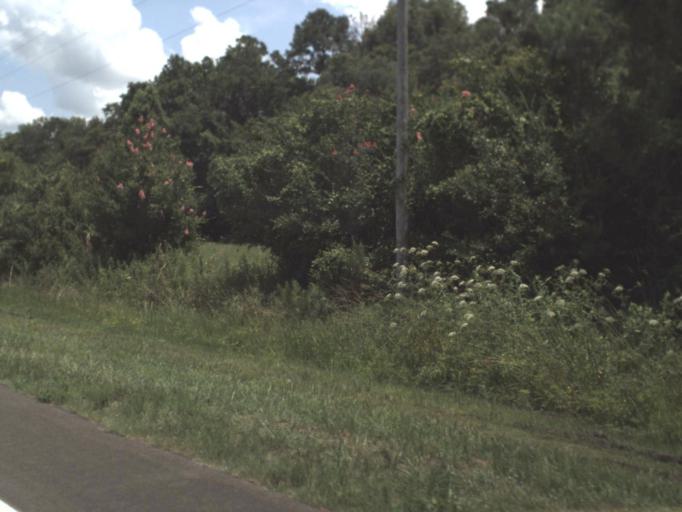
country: US
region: Florida
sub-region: Alachua County
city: Alachua
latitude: 29.8048
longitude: -82.3853
